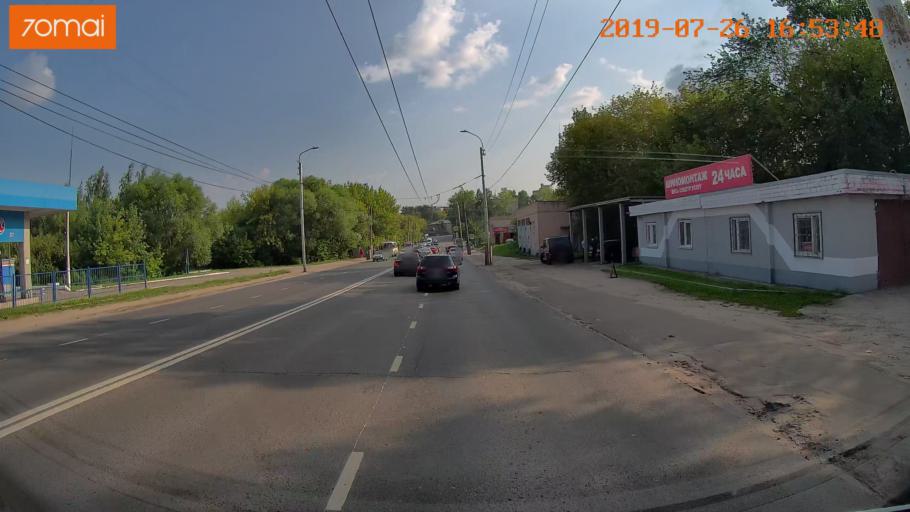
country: RU
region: Ivanovo
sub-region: Gorod Ivanovo
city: Ivanovo
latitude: 57.0128
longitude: 41.0010
